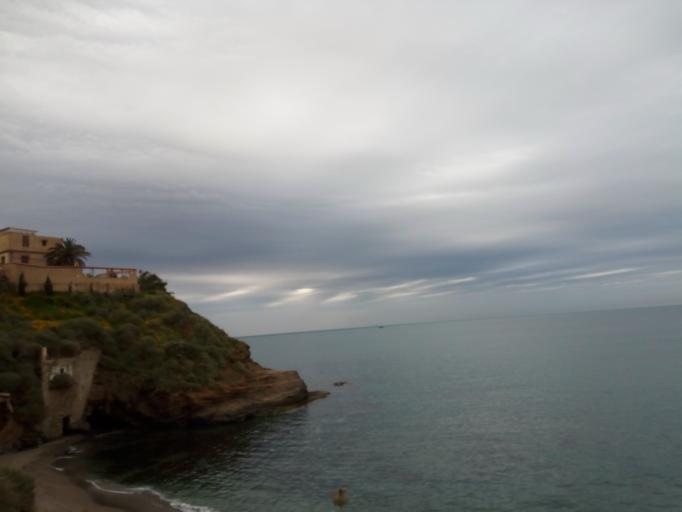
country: DZ
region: Alger
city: Algiers
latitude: 36.8125
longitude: 3.0222
